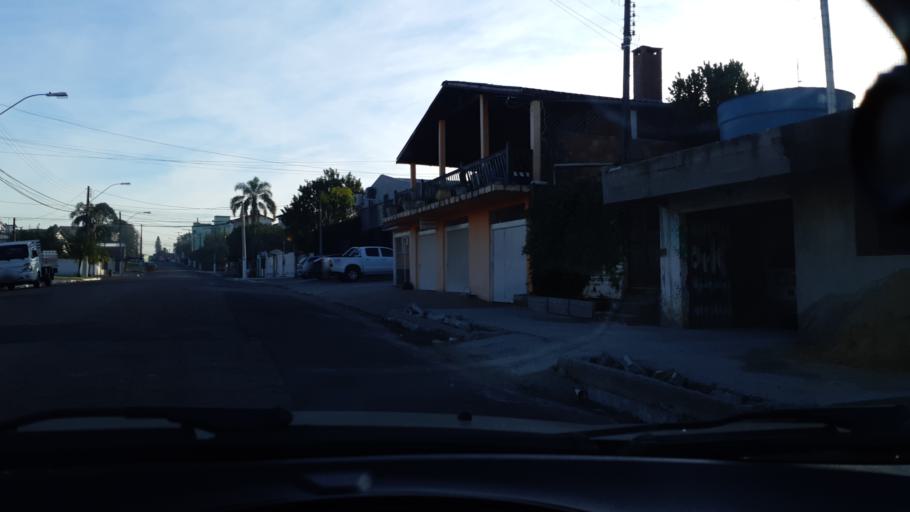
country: BR
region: Rio Grande do Sul
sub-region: Sapucaia Do Sul
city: Sapucaia
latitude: -29.8479
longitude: -51.1526
